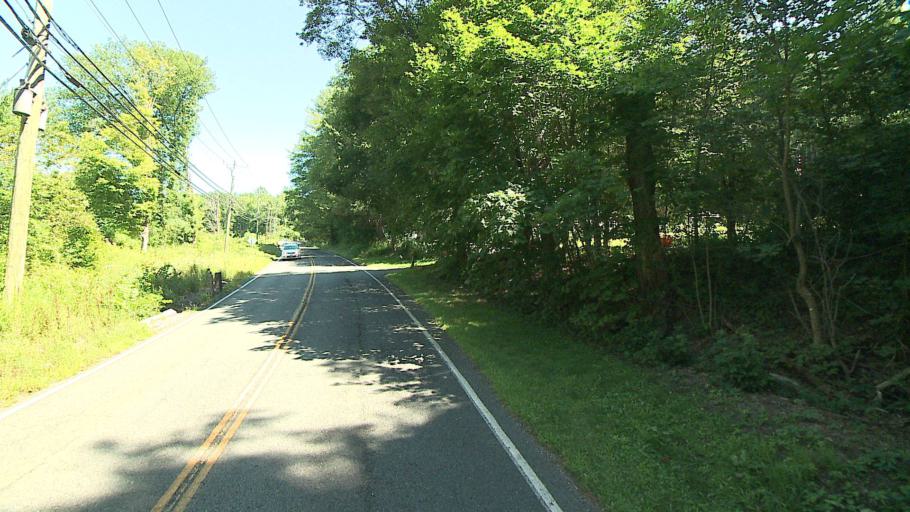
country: US
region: Connecticut
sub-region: Litchfield County
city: New Hartford Center
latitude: 41.9135
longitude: -72.9846
